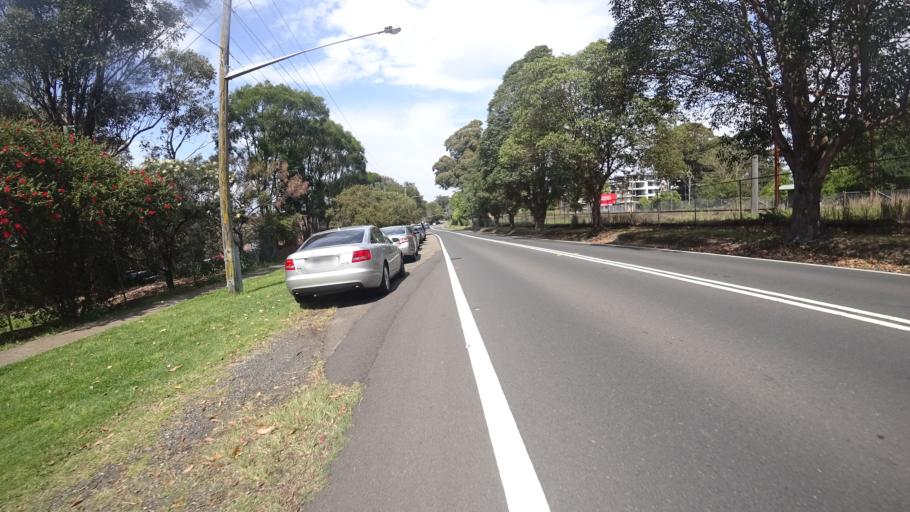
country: AU
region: New South Wales
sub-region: Hornsby Shire
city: Mount Colah
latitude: -33.6827
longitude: 151.1116
